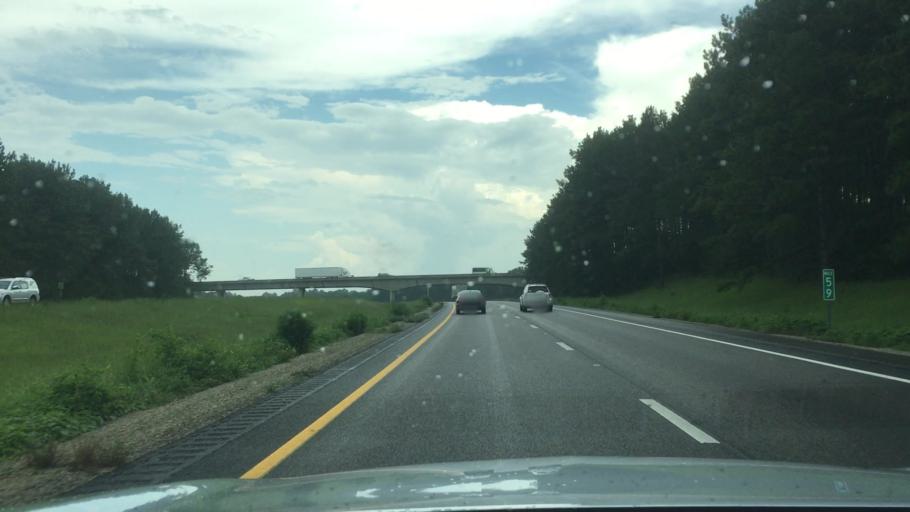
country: US
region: Mississippi
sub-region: Forrest County
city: Hattiesburg
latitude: 31.2380
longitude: -89.3226
